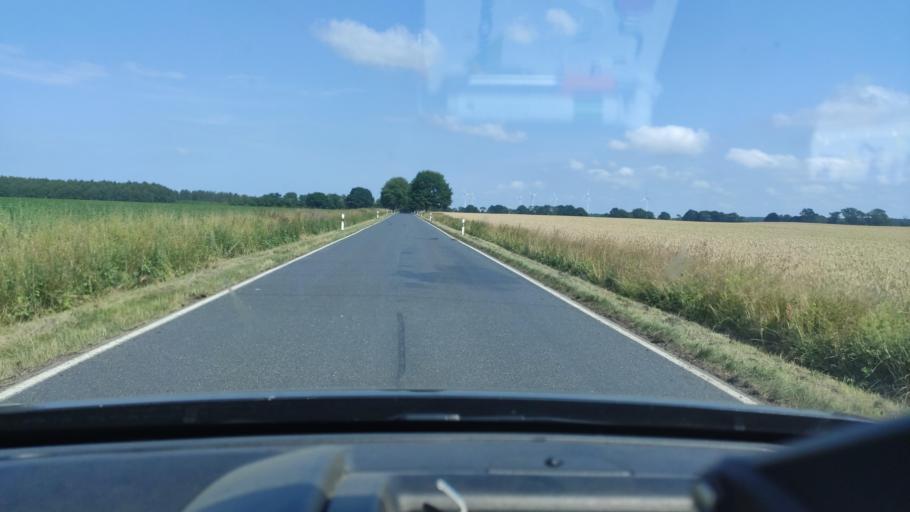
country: DE
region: Mecklenburg-Vorpommern
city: Grimmen
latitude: 54.0496
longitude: 13.0716
